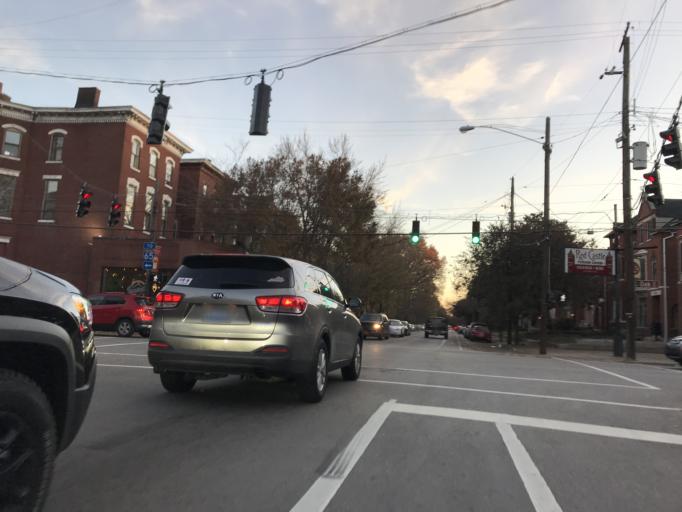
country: US
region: Kentucky
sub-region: Jefferson County
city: Louisville
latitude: 38.2348
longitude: -85.7554
